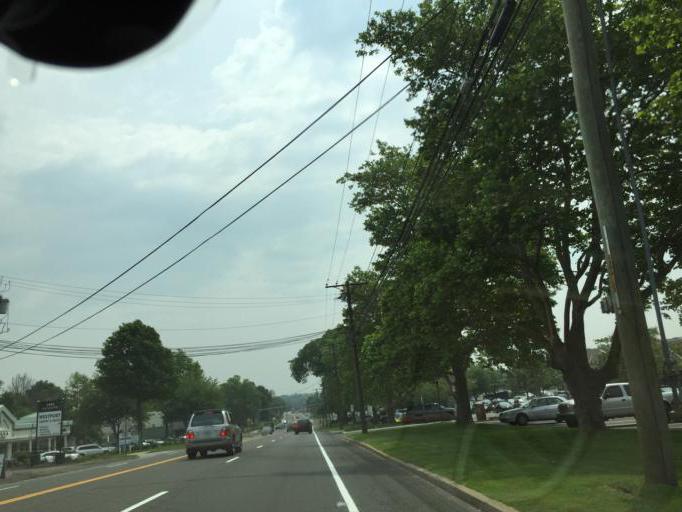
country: US
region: Connecticut
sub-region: Fairfield County
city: Southport
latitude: 41.1383
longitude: -73.3027
